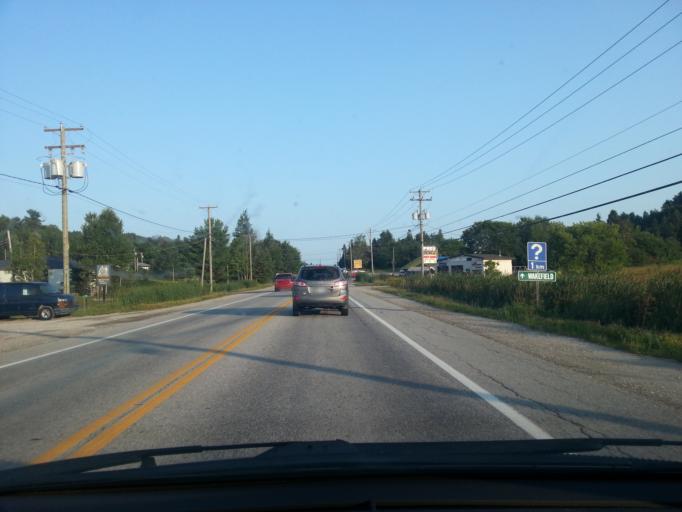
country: CA
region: Quebec
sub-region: Outaouais
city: Wakefield
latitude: 45.6195
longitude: -75.9240
